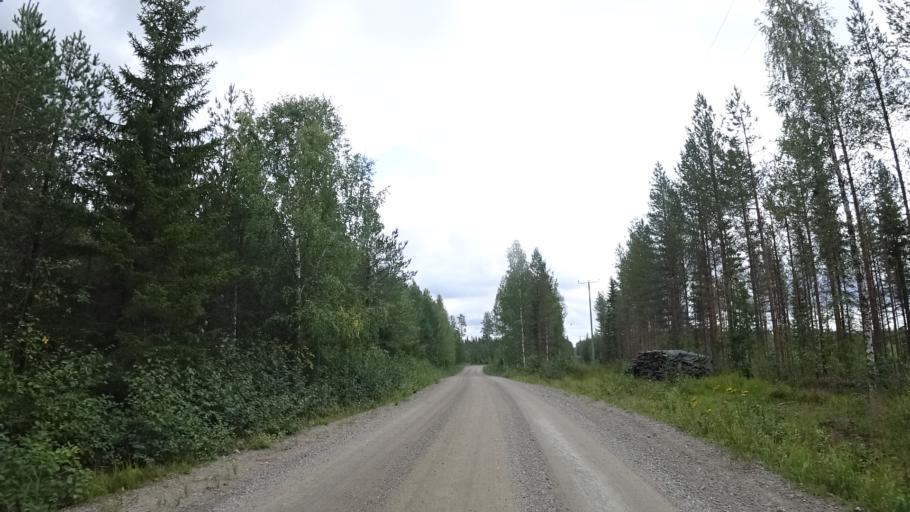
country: FI
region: North Karelia
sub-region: Joensuu
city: Ilomantsi
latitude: 62.9282
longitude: 31.3256
